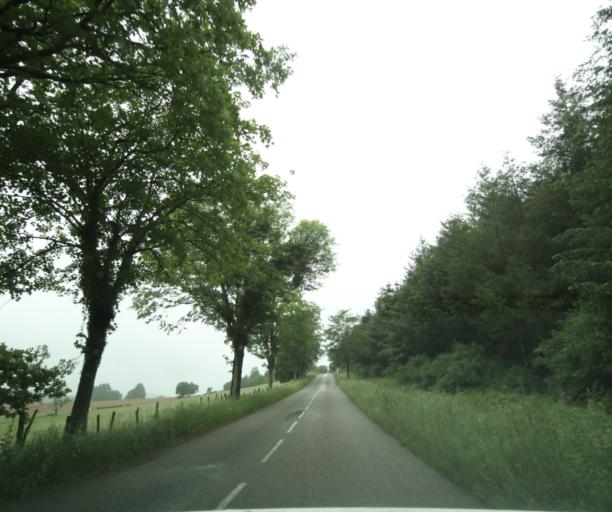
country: FR
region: Bourgogne
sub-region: Departement de Saone-et-Loire
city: Charolles
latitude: 46.4413
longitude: 4.3995
